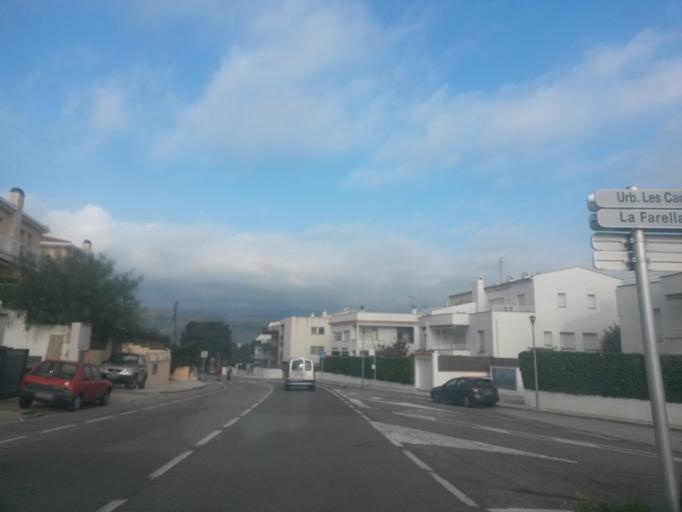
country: ES
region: Catalonia
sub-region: Provincia de Girona
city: Llanca
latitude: 42.3667
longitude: 3.1604
